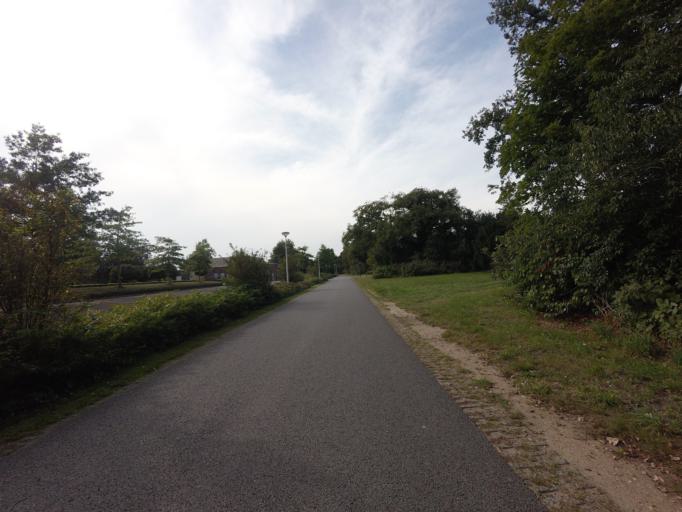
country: NL
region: Gelderland
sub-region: Gemeente Lochem
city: Laren
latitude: 52.2840
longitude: 6.4098
